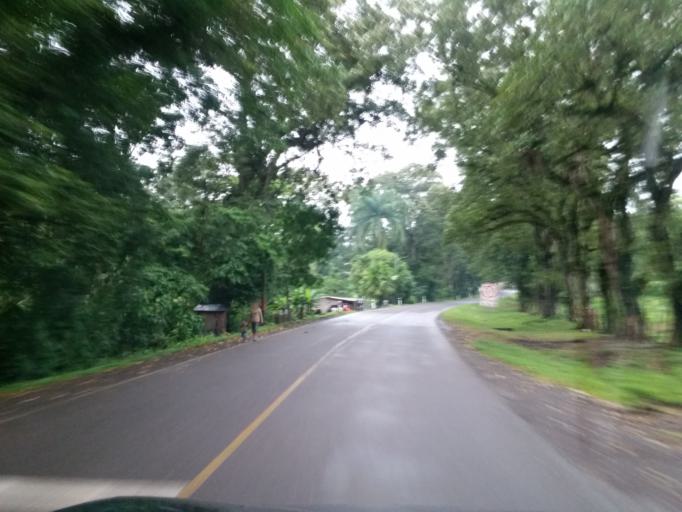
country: NI
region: Matagalpa
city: San Ramon
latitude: 13.1180
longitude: -85.7491
